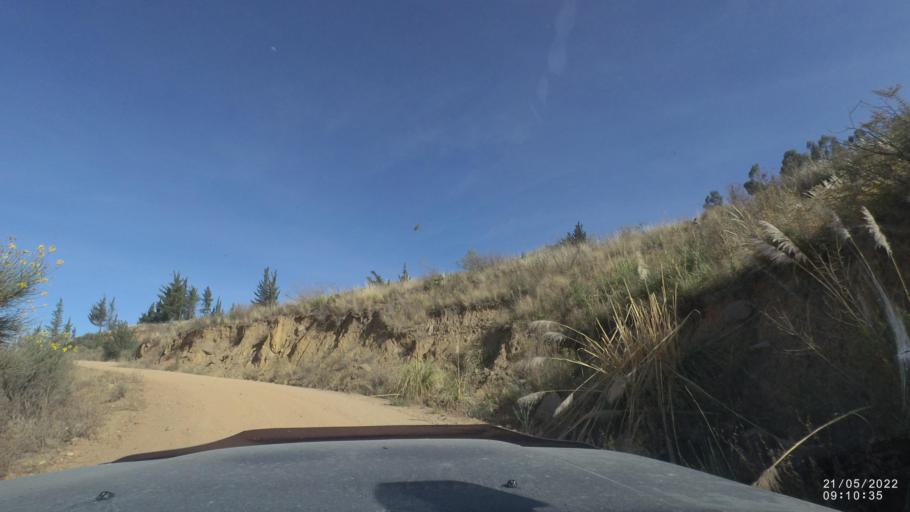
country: BO
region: Cochabamba
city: Cochabamba
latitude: -17.3717
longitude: -66.0212
